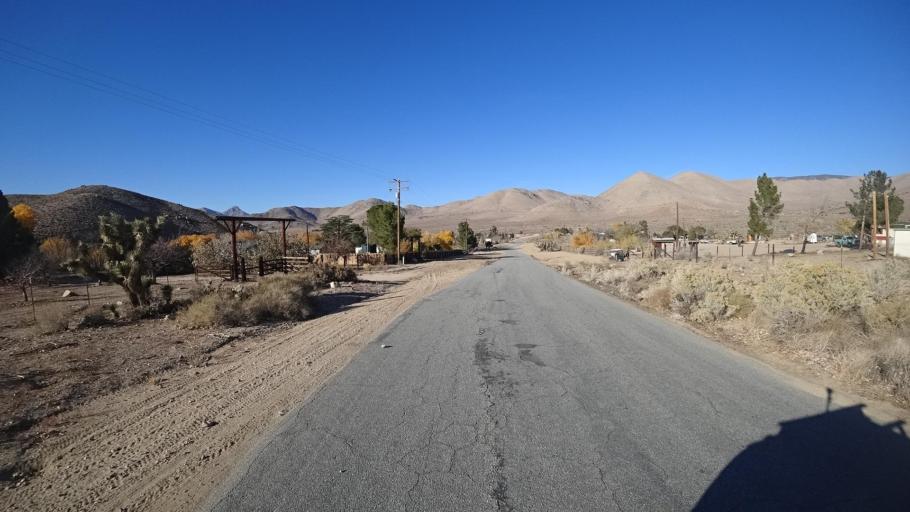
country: US
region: California
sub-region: Kern County
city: Weldon
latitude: 35.5426
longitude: -118.2070
